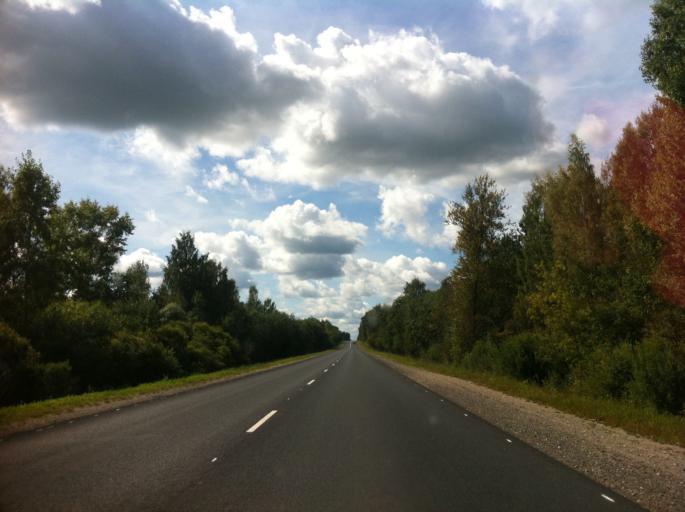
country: RU
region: Pskov
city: Izborsk
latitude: 57.7229
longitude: 27.9434
